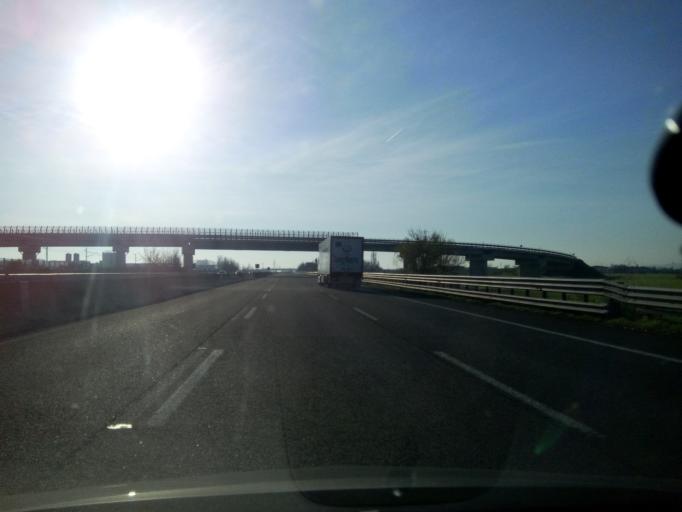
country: IT
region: Emilia-Romagna
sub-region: Provincia di Reggio Emilia
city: Praticello
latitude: 44.8023
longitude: 10.4446
